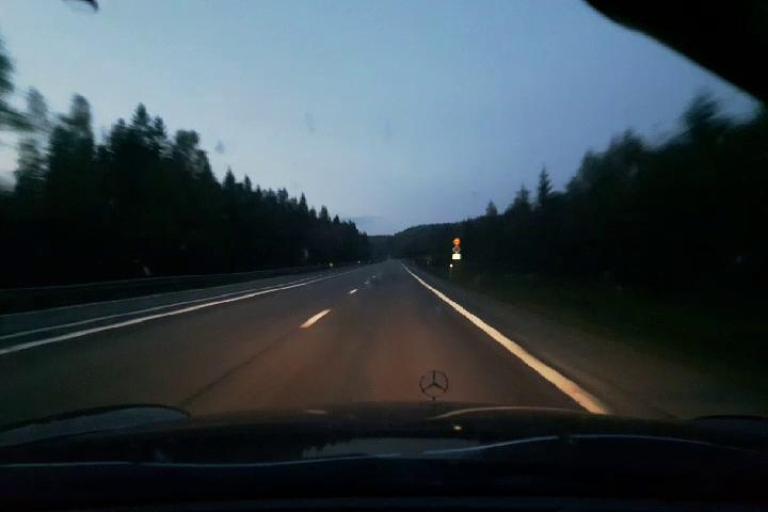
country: SE
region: Vaesternorrland
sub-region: Kramfors Kommun
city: Nordingra
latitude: 63.0765
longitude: 18.3631
